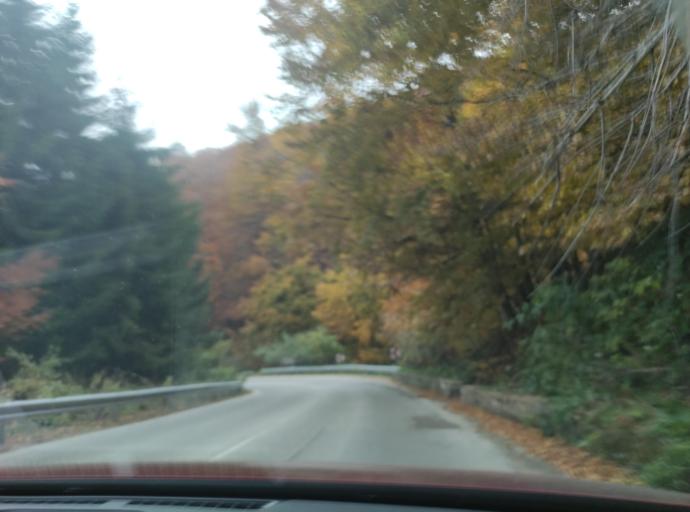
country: BG
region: Montana
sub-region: Obshtina Berkovitsa
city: Berkovitsa
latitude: 43.1287
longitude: 23.1409
